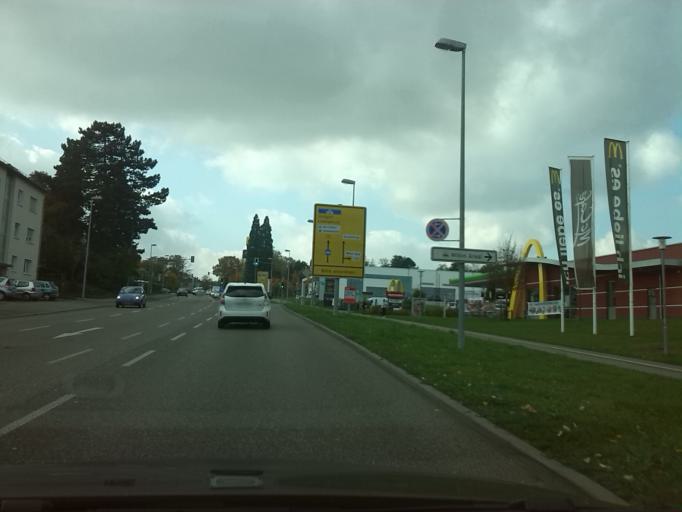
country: DE
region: Baden-Wuerttemberg
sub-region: Regierungsbezirk Stuttgart
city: Kornwestheim
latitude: 48.8670
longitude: 9.2008
